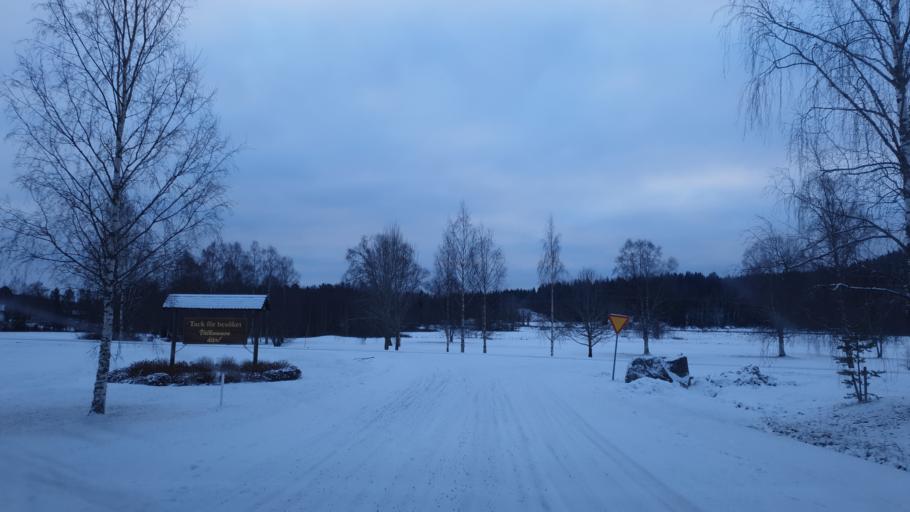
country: SE
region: Gaevleborg
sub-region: Bollnas Kommun
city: Kilafors
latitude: 61.2566
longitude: 16.5379
